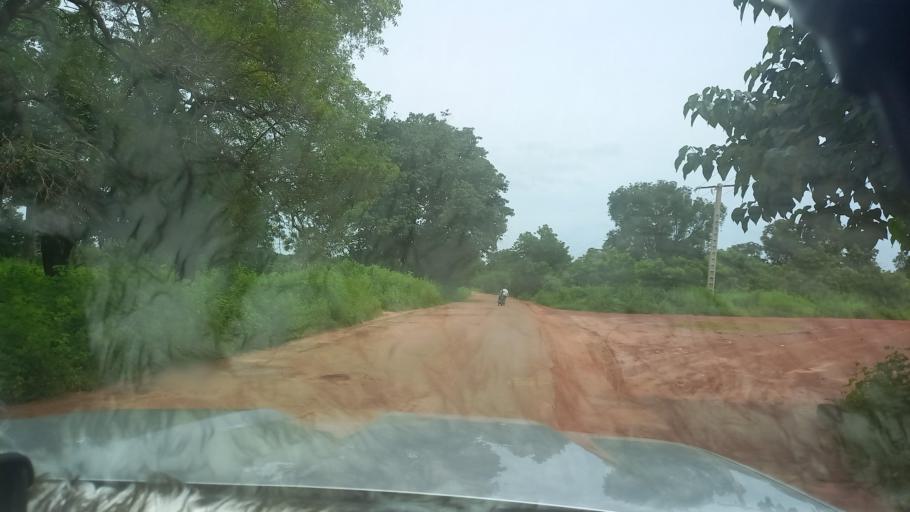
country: SN
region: Kolda
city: Marsassoum
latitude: 12.9090
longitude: -16.0125
